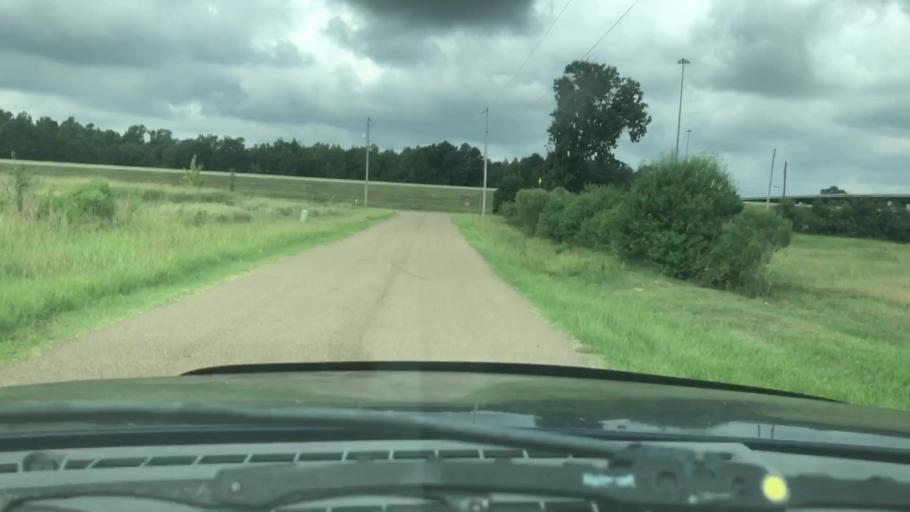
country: US
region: Texas
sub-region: Bowie County
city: Wake Village
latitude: 33.3915
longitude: -94.0955
